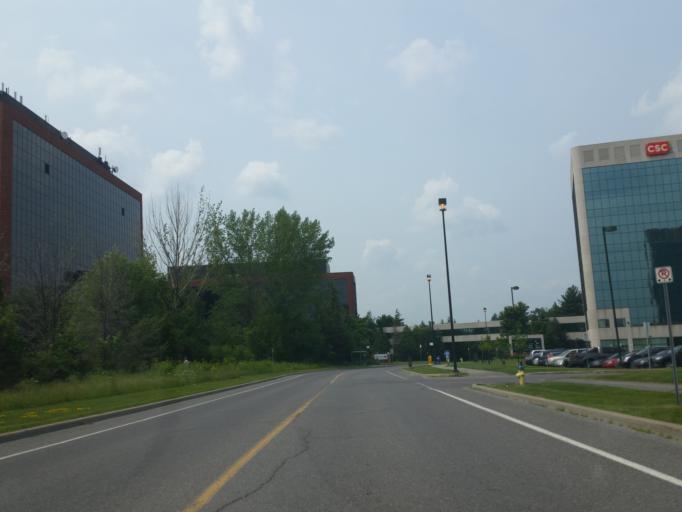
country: CA
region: Ontario
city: Bells Corners
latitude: 45.3476
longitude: -75.9195
